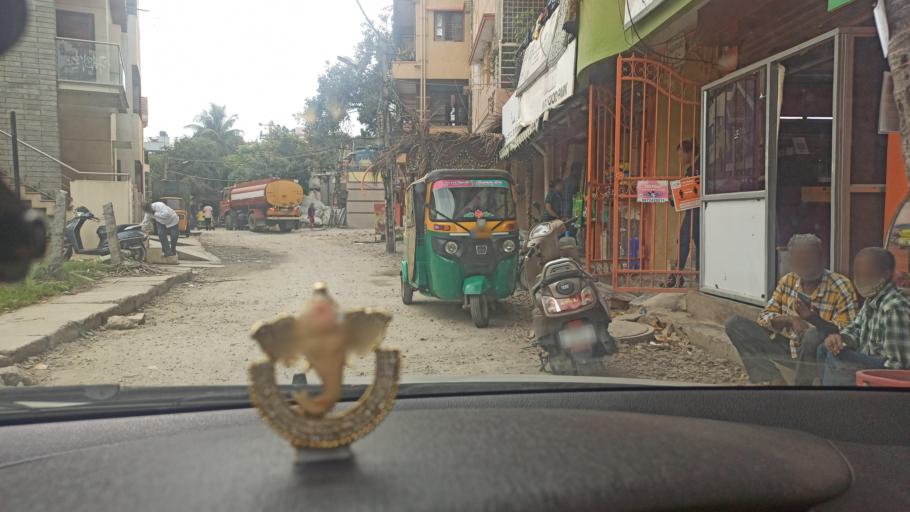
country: IN
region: Karnataka
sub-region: Bangalore Urban
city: Bangalore
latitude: 12.9194
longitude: 77.6370
